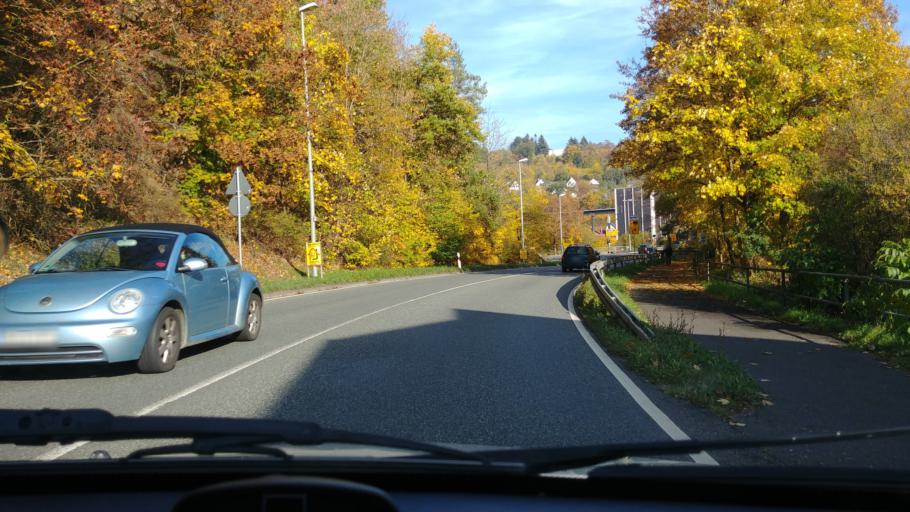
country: DE
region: Rheinland-Pfalz
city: Schiesheim
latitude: 50.2425
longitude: 8.0629
